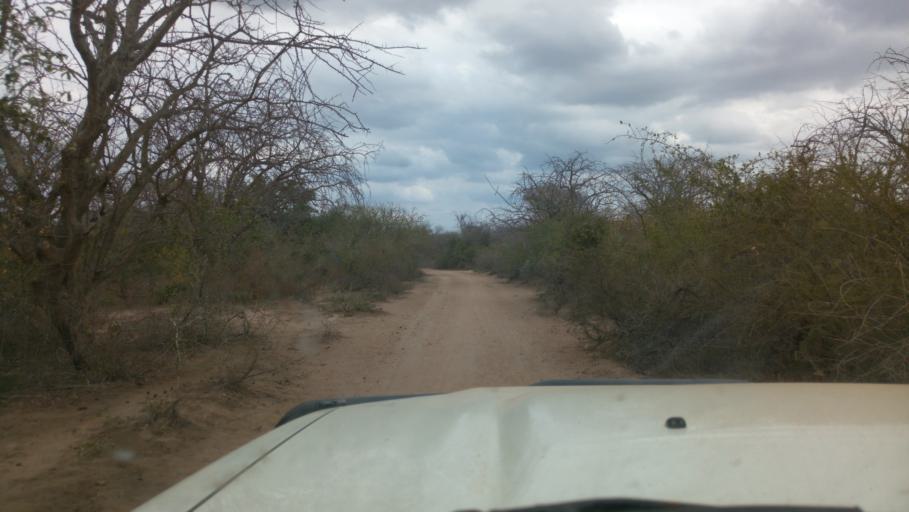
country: KE
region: Kitui
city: Kitui
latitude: -1.8299
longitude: 38.4462
